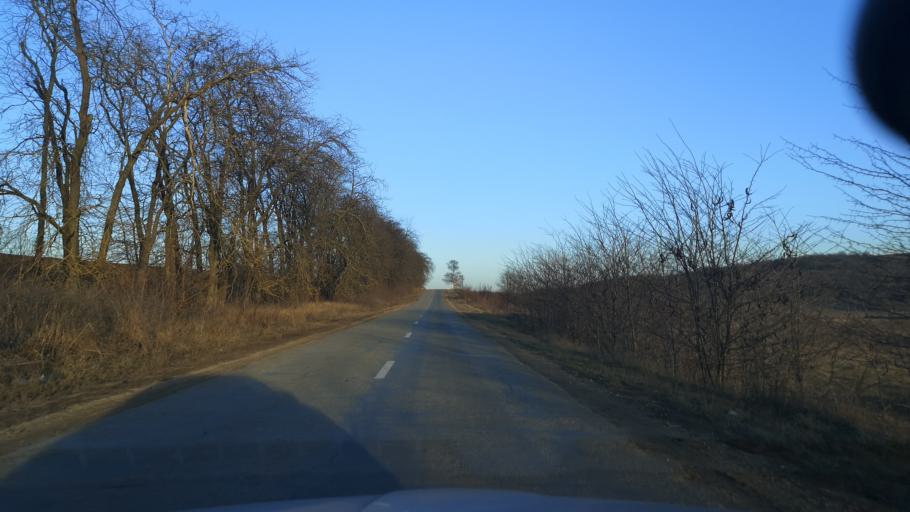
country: MD
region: Orhei
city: Orhei
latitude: 47.2974
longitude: 28.9064
